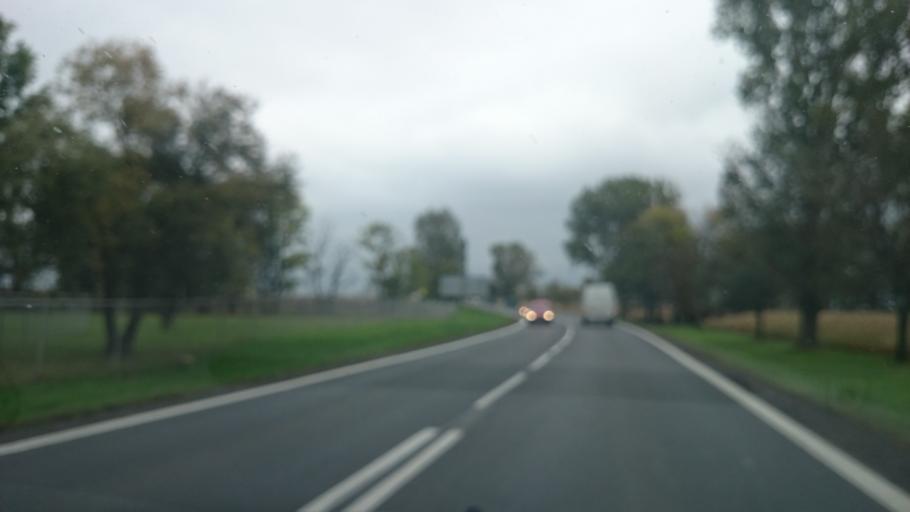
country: PL
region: Lower Silesian Voivodeship
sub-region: Powiat wroclawski
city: Kobierzyce
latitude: 50.9544
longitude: 16.9144
